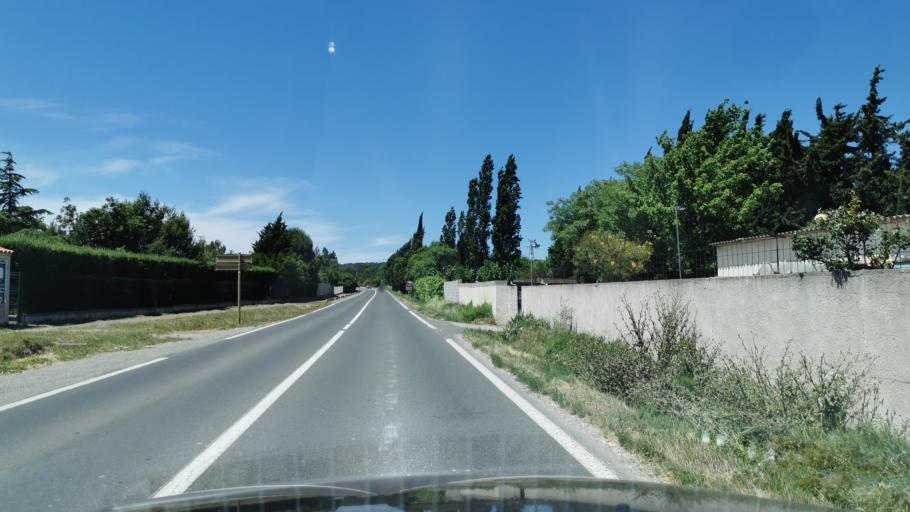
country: FR
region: Languedoc-Roussillon
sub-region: Departement de l'Aude
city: Narbonne
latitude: 43.1965
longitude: 2.9769
